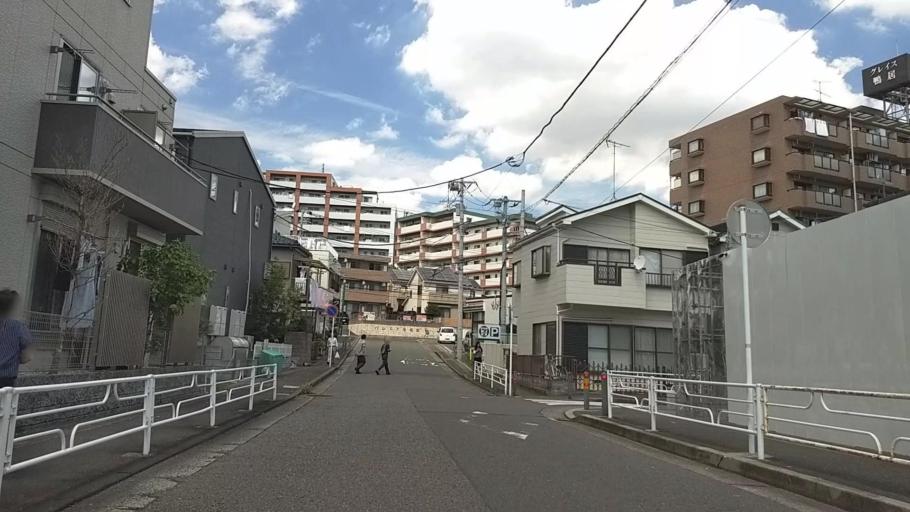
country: JP
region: Kanagawa
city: Yokohama
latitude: 35.5184
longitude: 139.5631
